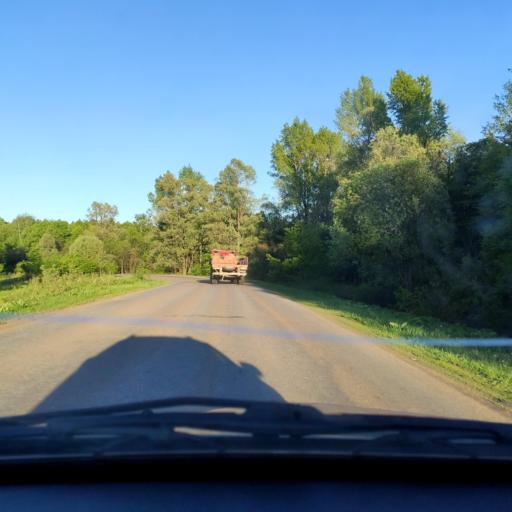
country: RU
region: Bashkortostan
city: Blagoveshchensk
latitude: 55.0312
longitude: 56.1064
